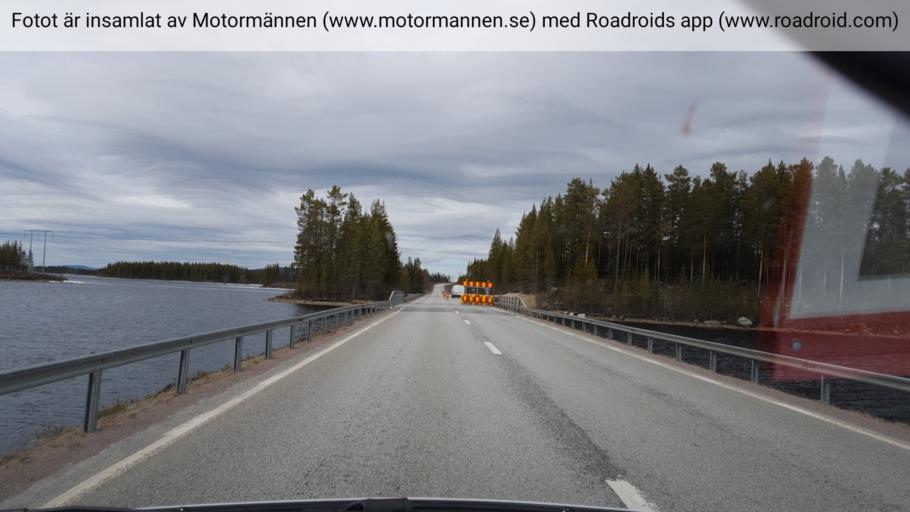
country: SE
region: Vaesterbotten
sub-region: Asele Kommun
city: Asele
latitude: 63.9032
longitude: 17.2210
